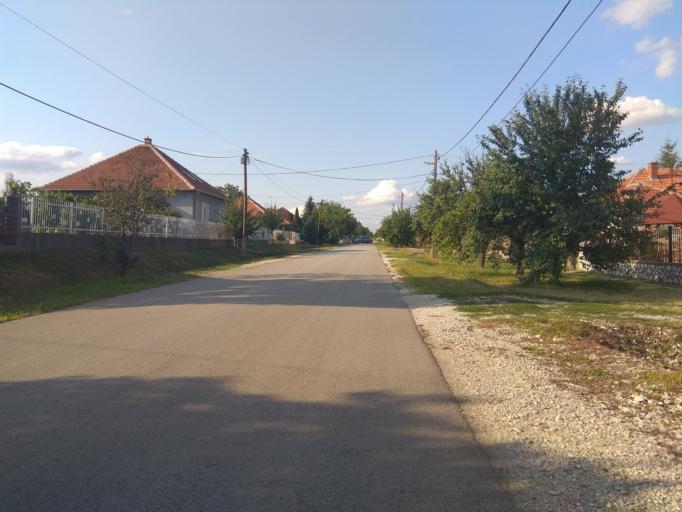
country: HU
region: Borsod-Abauj-Zemplen
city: Emod
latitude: 47.9316
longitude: 20.8076
